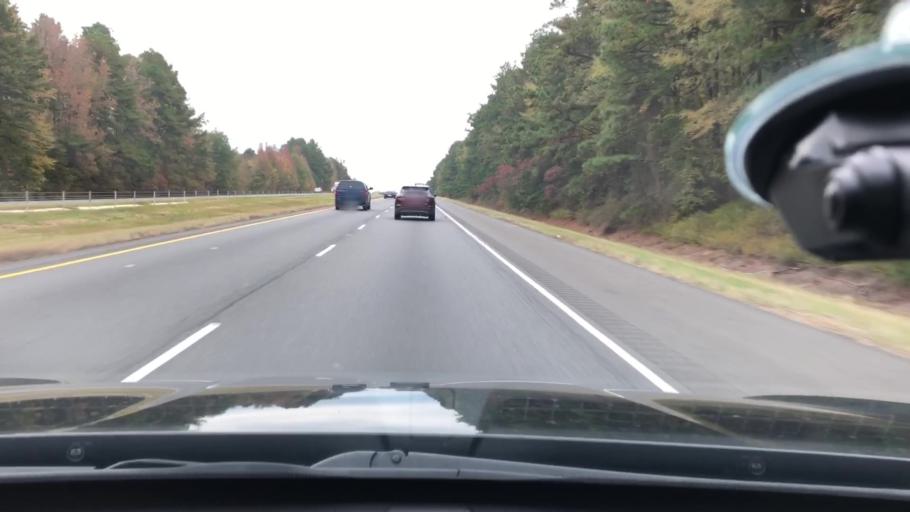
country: US
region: Arkansas
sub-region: Clark County
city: Gurdon
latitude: 34.0299
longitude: -93.1495
